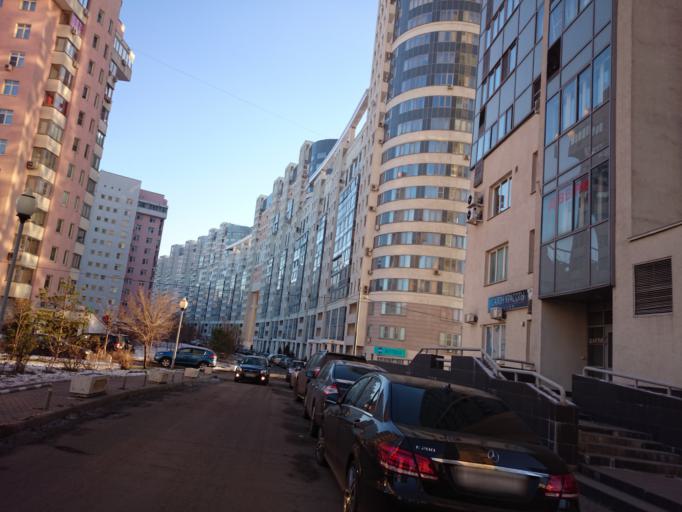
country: RU
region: Moscow
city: Sokol
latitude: 55.7870
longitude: 37.5205
